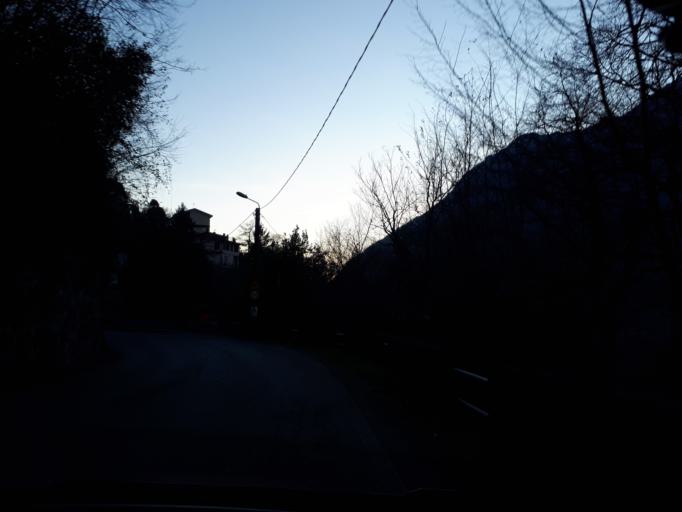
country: IT
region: Lombardy
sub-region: Provincia di Como
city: Nesso
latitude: 45.9022
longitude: 9.1544
